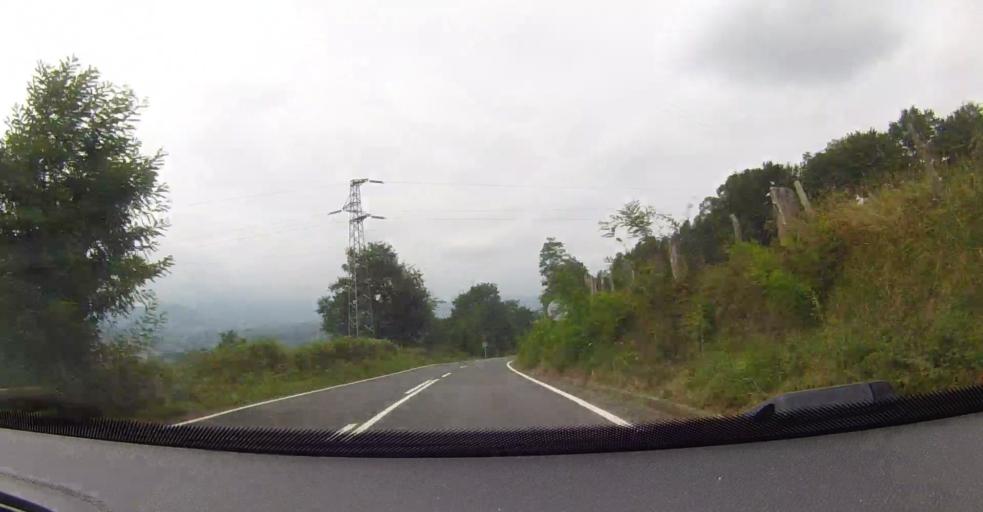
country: ES
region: Basque Country
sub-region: Bizkaia
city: Balmaseda
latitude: 43.2393
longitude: -3.3106
